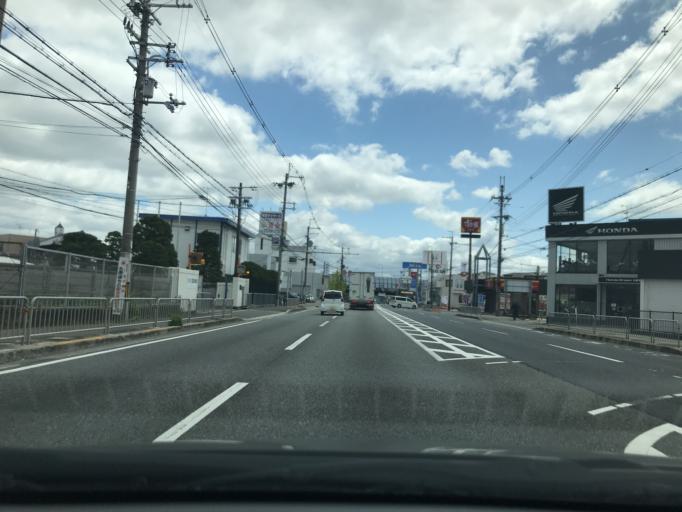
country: JP
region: Osaka
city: Ibaraki
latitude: 34.8335
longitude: 135.5578
